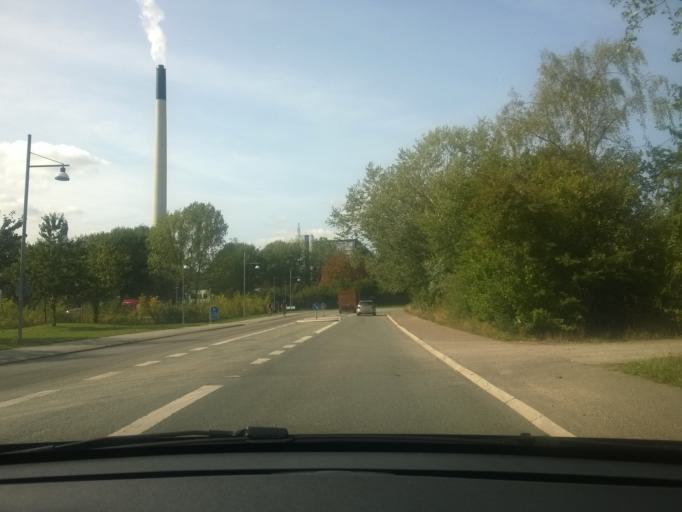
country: DK
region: Capital Region
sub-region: Herlev Kommune
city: Herlev
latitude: 55.7055
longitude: 12.4255
